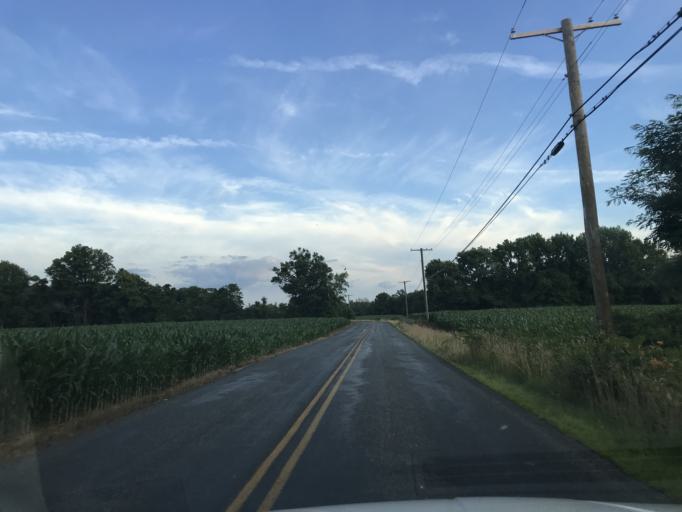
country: US
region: Maryland
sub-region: Harford County
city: Riverside
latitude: 39.5373
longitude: -76.2255
